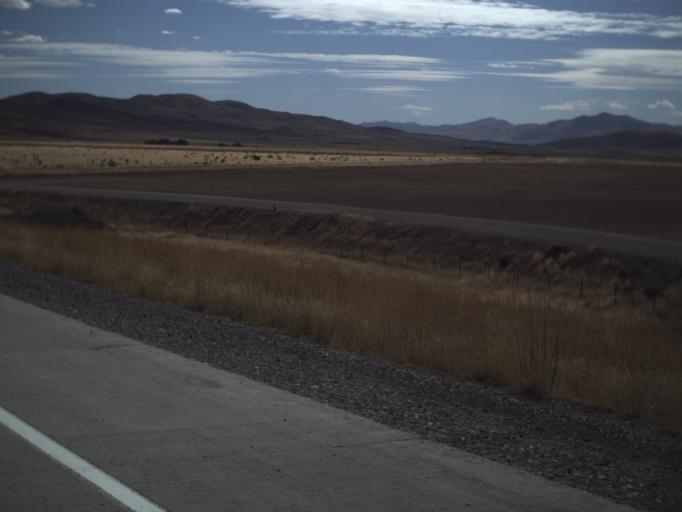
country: US
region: Utah
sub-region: Box Elder County
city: Garland
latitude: 41.8175
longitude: -112.4143
